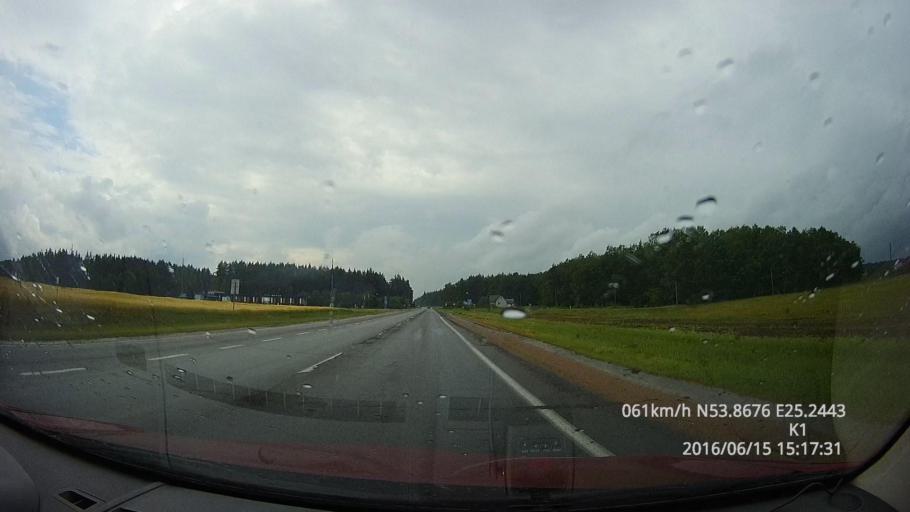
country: BY
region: Grodnenskaya
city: Lida
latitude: 53.8676
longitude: 25.2440
